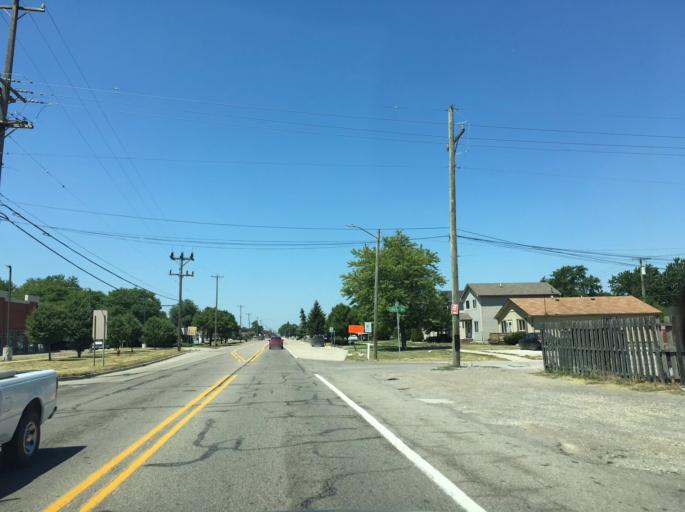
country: US
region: Michigan
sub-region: Macomb County
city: Fraser
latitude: 42.5397
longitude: -82.9097
